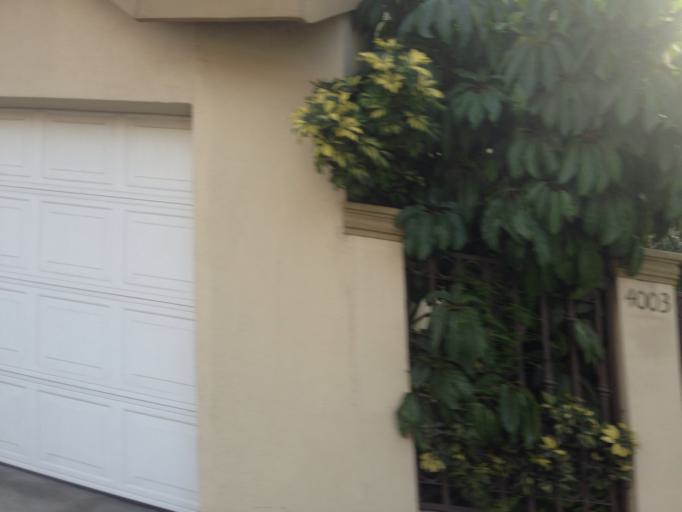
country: MX
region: Baja California
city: Tijuana
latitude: 32.4956
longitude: -117.0016
